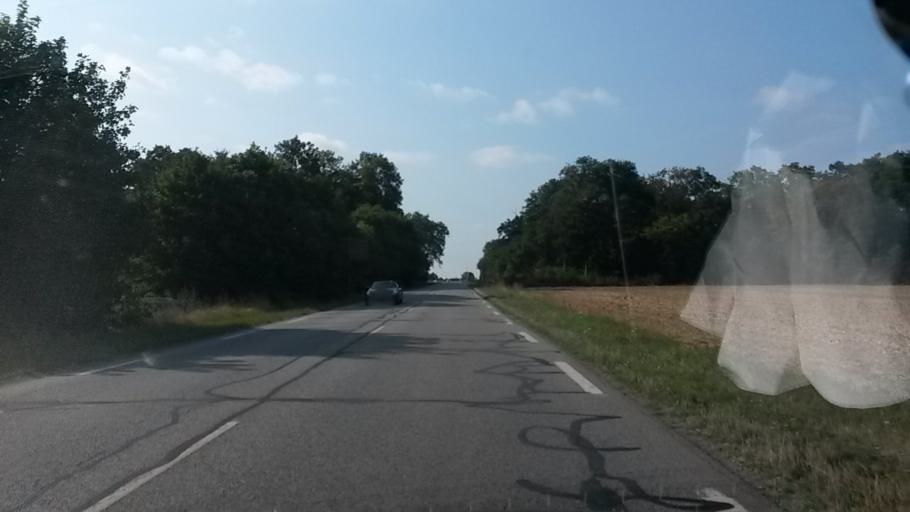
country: FR
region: Haute-Normandie
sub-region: Departement de l'Eure
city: Evreux
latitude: 48.9895
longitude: 1.1565
